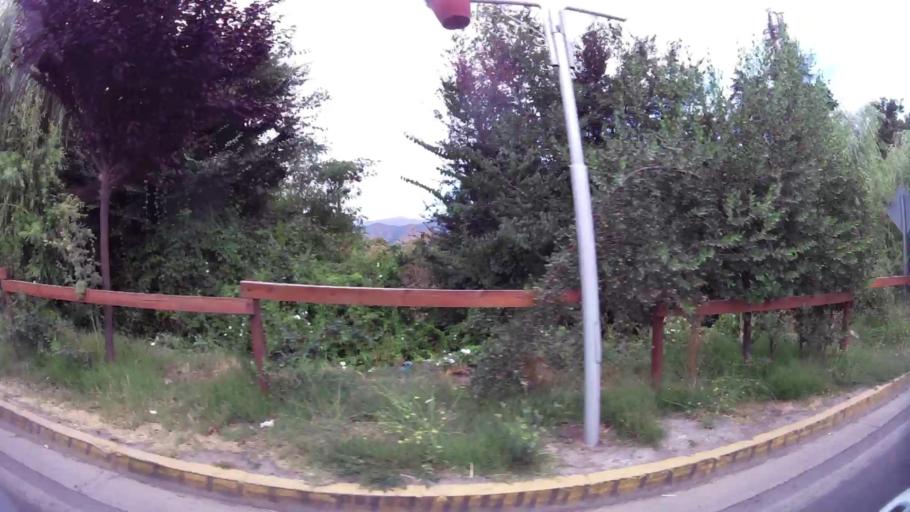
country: CL
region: O'Higgins
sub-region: Provincia de Cachapoal
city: Graneros
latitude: -34.0791
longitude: -70.7353
